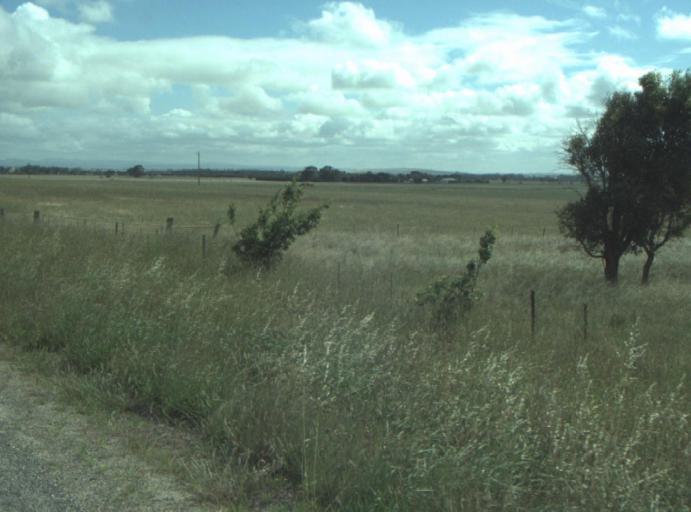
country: AU
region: Victoria
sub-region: Greater Geelong
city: Lara
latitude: -37.8651
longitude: 144.3243
